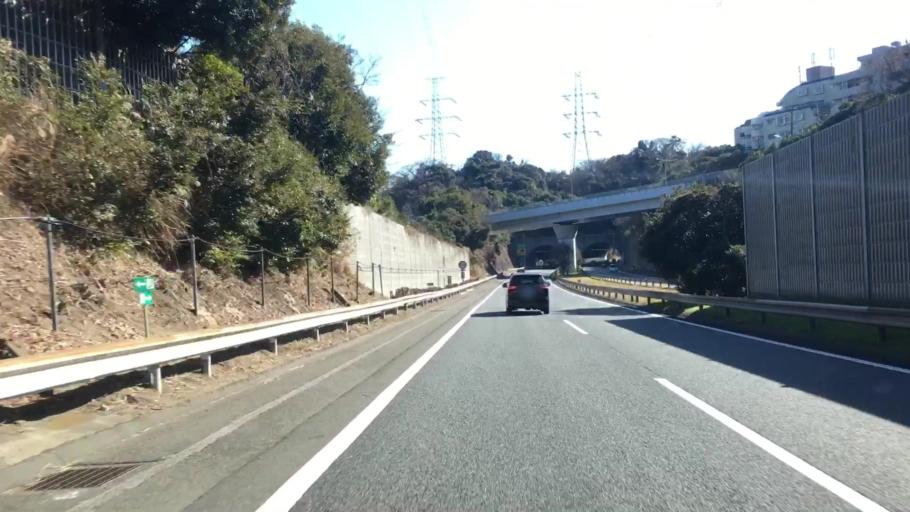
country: JP
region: Kanagawa
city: Zushi
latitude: 35.3252
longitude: 139.5991
